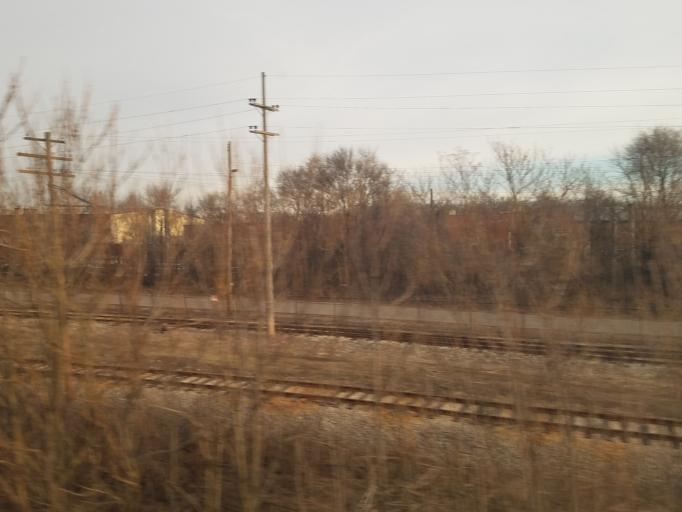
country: US
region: Indiana
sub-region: Saint Joseph County
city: South Bend
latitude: 41.6823
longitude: -86.3019
